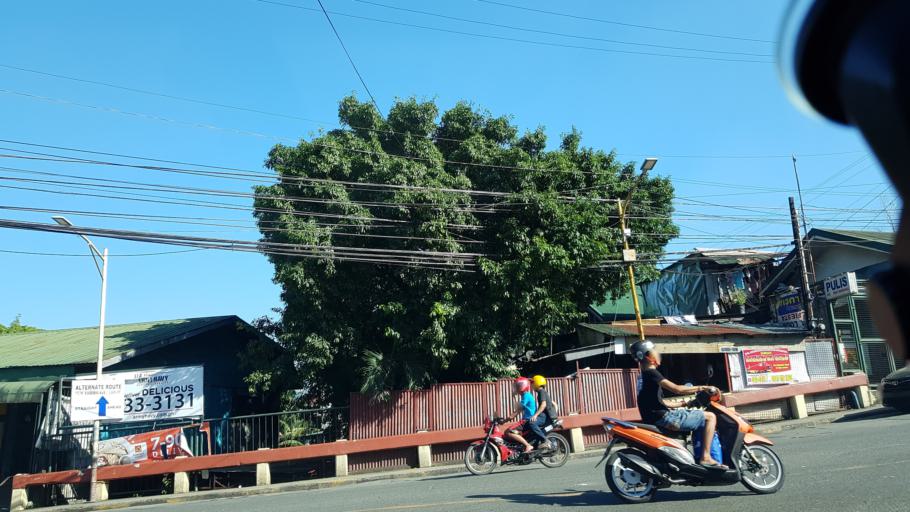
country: PH
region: Calabarzon
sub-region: Province of Rizal
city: Cainta
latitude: 14.5755
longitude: 121.0986
